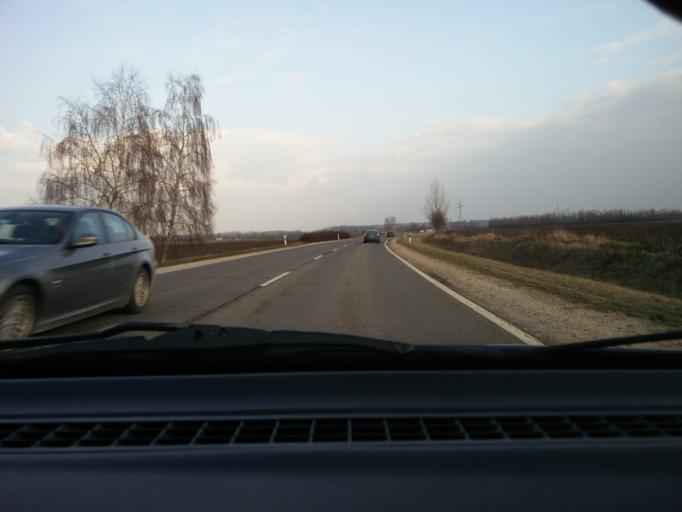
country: HU
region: Pest
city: Pilis
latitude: 47.2590
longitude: 19.5377
